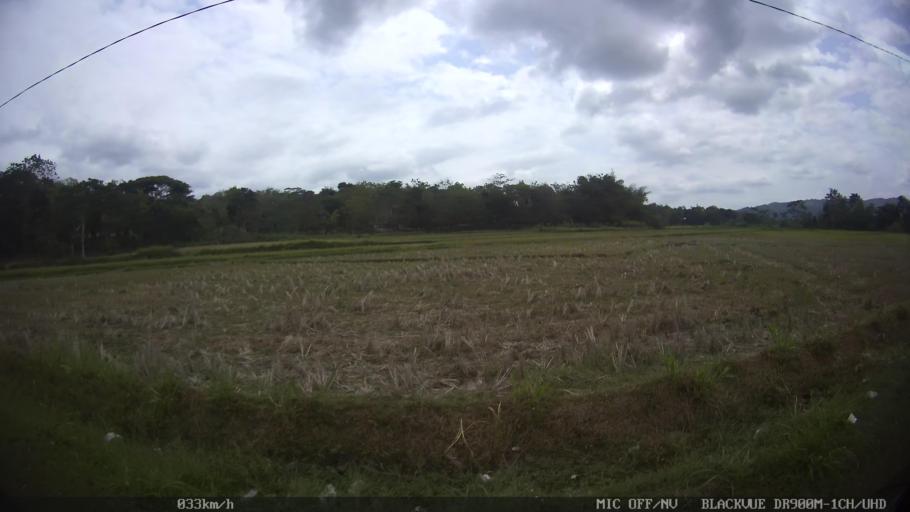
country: ID
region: Daerah Istimewa Yogyakarta
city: Depok
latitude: -7.8138
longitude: 110.4724
